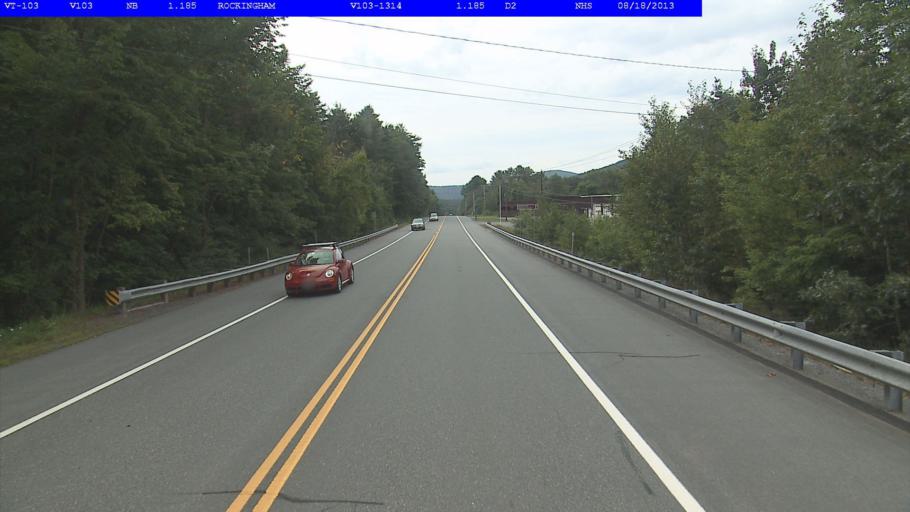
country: US
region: Vermont
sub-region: Windham County
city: Rockingham
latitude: 43.1857
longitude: -72.4796
